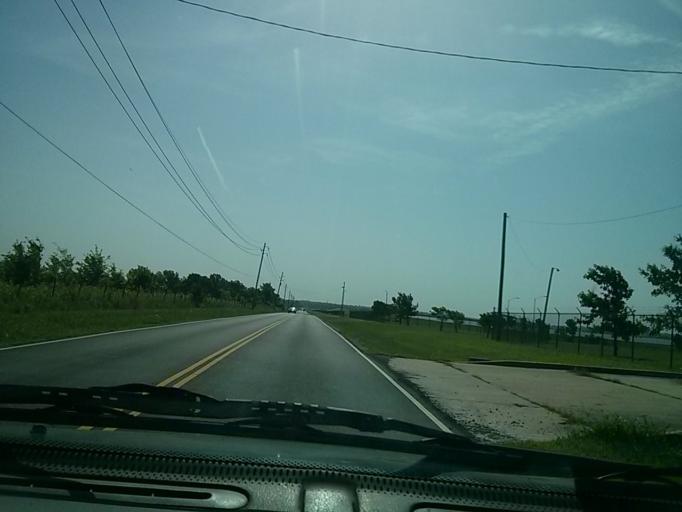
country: US
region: Oklahoma
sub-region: Rogers County
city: Catoosa
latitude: 36.1334
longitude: -95.7776
